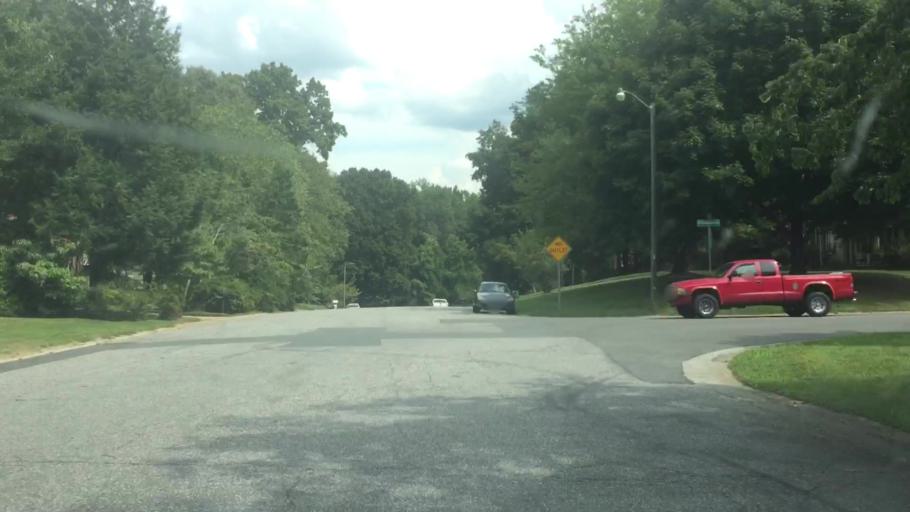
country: US
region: North Carolina
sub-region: Iredell County
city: Mooresville
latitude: 35.5563
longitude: -80.7994
